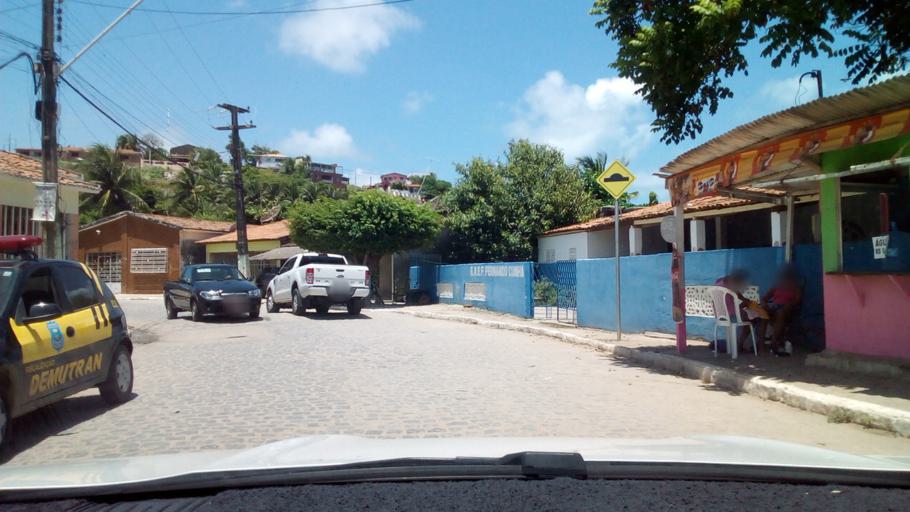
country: BR
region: Paraiba
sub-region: Pitimbu
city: Pitimbu
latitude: -7.4762
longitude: -34.8107
